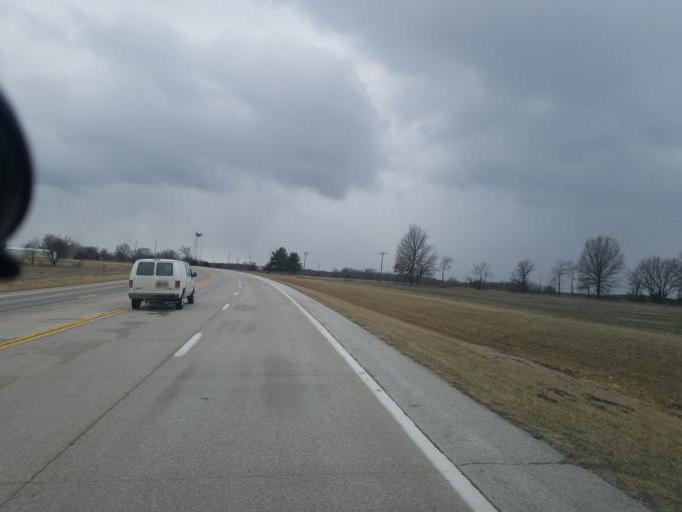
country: US
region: Missouri
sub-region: Macon County
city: Macon
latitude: 39.7859
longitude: -92.4818
